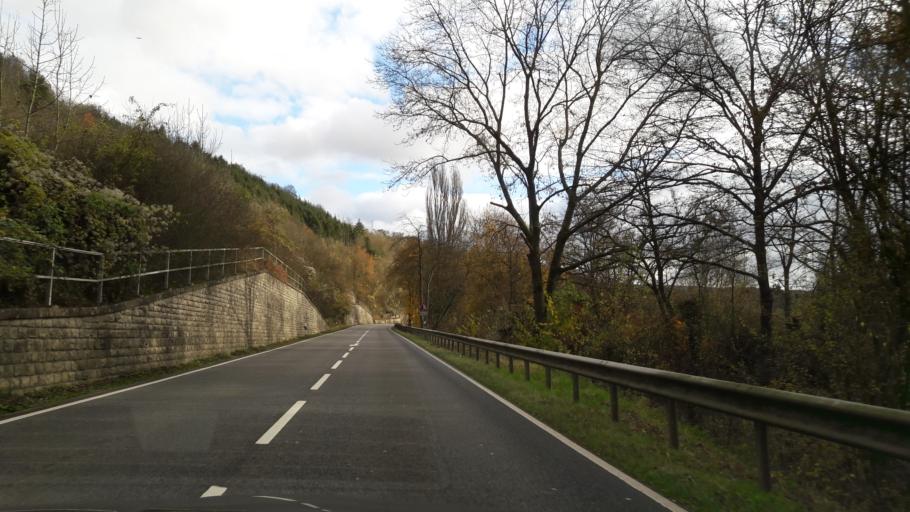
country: DE
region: Rheinland-Pfalz
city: Ralingen
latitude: 49.8108
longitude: 6.5040
